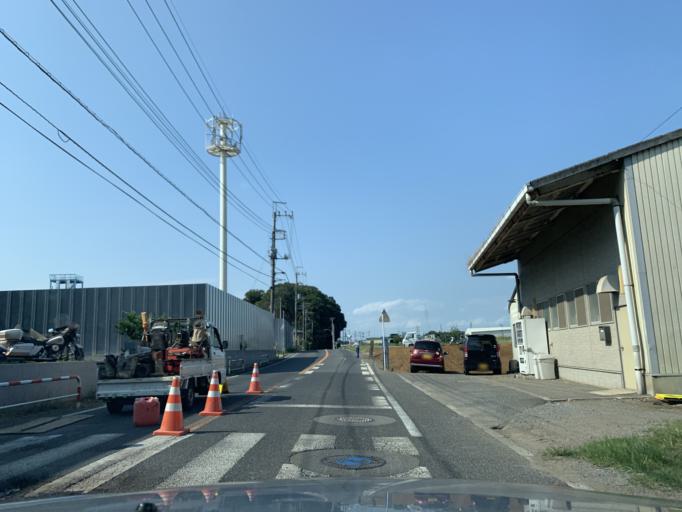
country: JP
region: Chiba
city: Nagareyama
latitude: 35.8457
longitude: 139.9345
